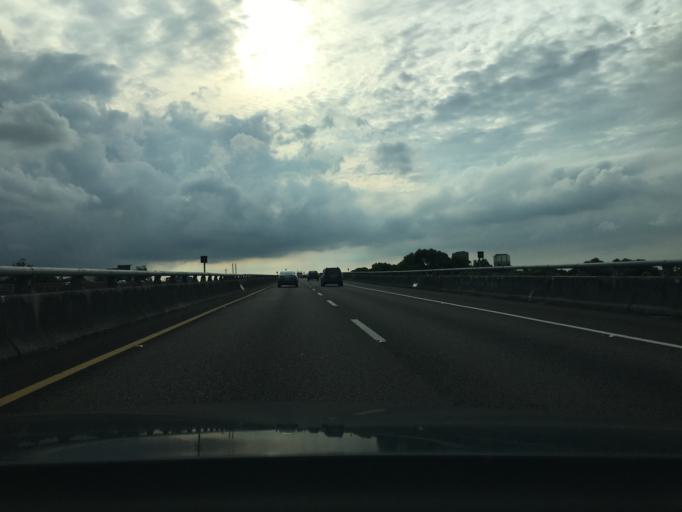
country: TW
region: Taiwan
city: Daxi
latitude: 24.9313
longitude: 121.1809
